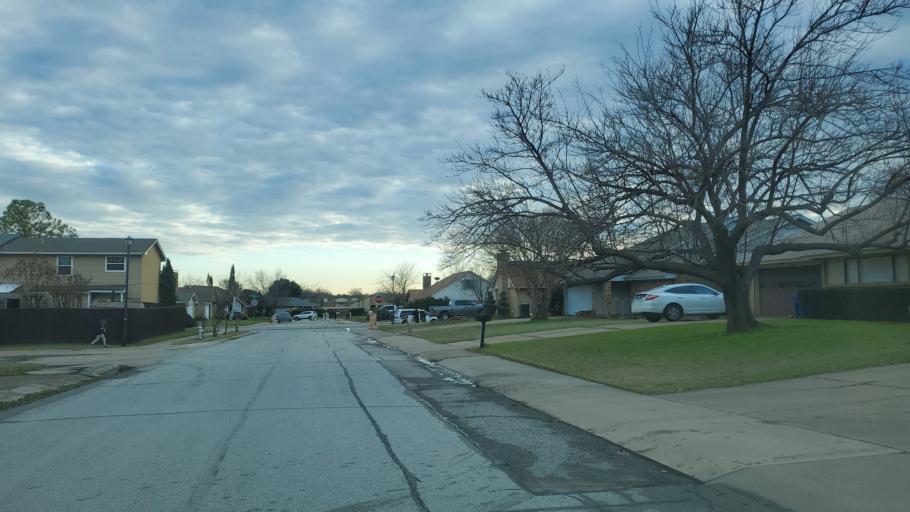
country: US
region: Texas
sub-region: Dallas County
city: Carrollton
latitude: 32.9880
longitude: -96.8795
